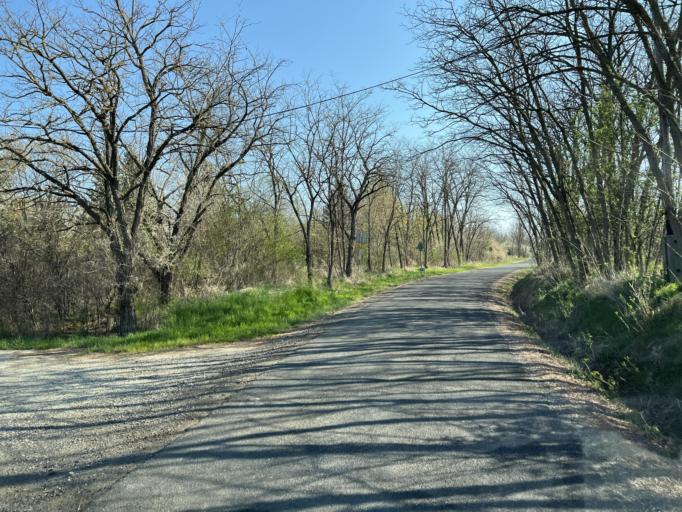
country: SK
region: Nitriansky
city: Sahy
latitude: 48.0274
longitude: 18.8286
